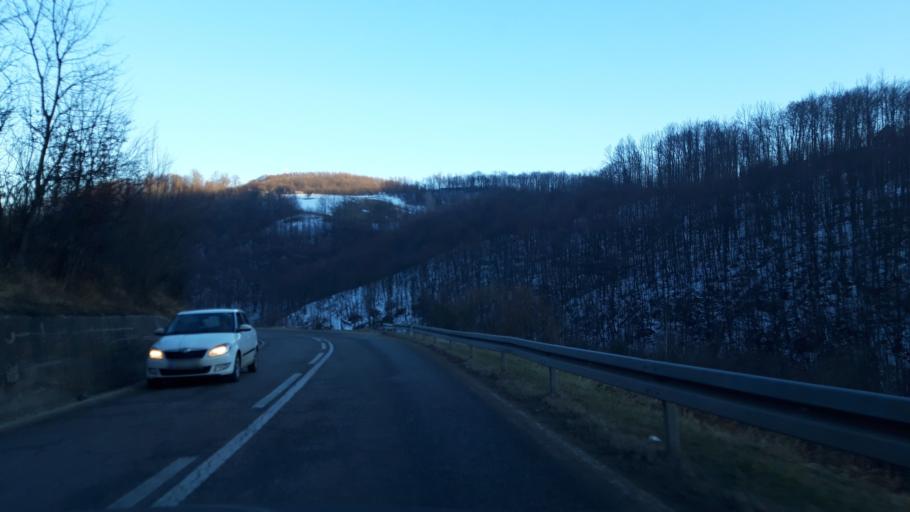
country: BA
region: Republika Srpska
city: Vlasenica
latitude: 44.1806
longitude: 18.9790
